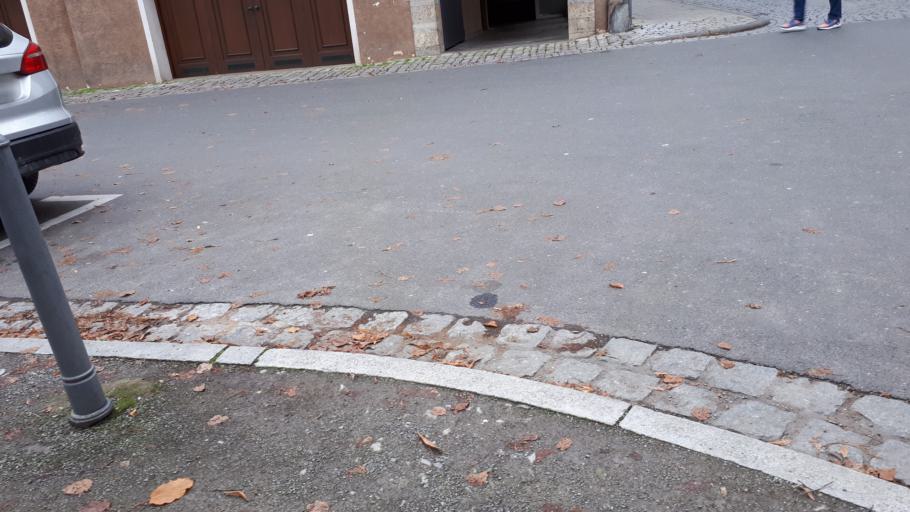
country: DE
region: Bavaria
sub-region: Regierungsbezirk Unterfranken
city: Kitzingen
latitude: 49.7368
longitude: 10.1642
